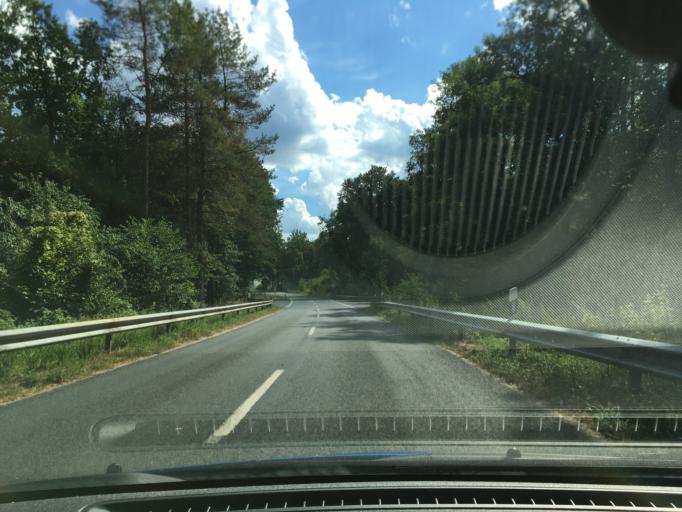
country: DE
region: Lower Saxony
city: Rehlingen
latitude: 53.0915
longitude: 10.2038
